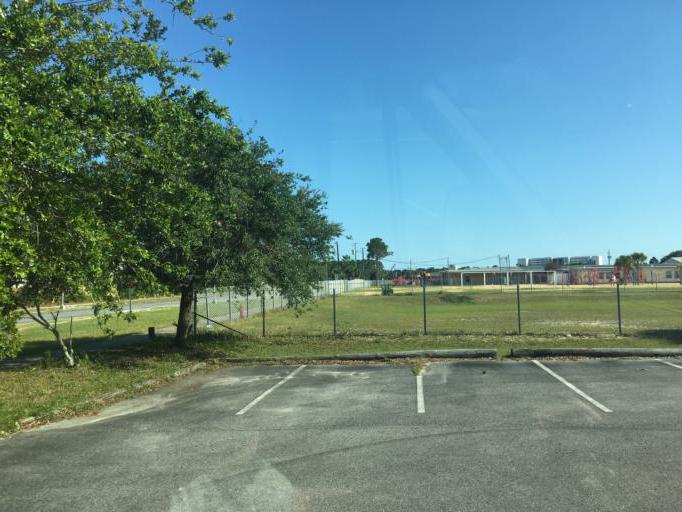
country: US
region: Florida
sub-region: Bay County
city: Panama City Beach
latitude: 30.2013
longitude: -85.8363
